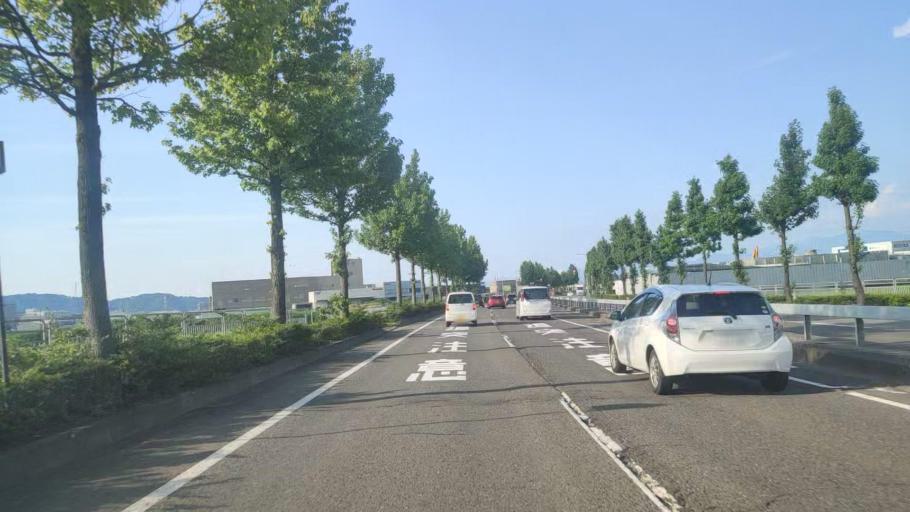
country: JP
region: Fukui
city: Fukui-shi
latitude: 36.0168
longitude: 136.2106
